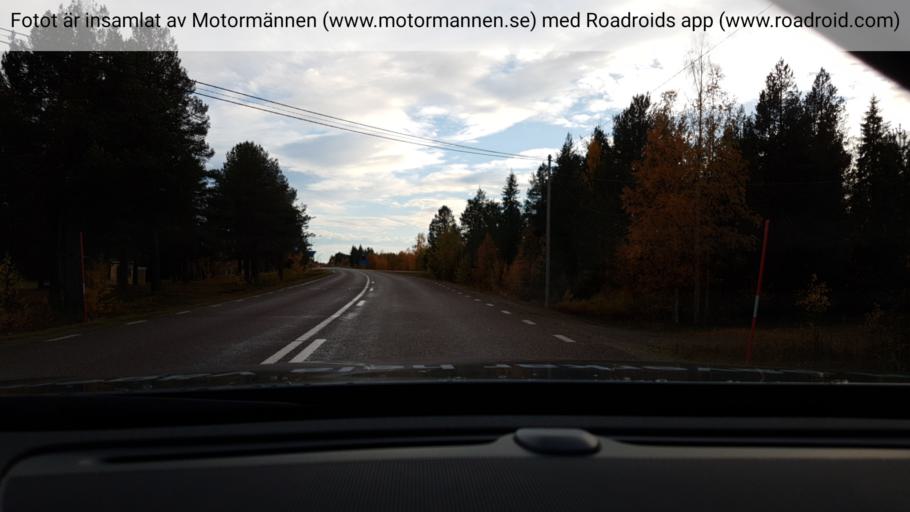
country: SE
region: Norrbotten
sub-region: Pajala Kommun
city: Pajala
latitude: 67.1631
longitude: 22.6337
